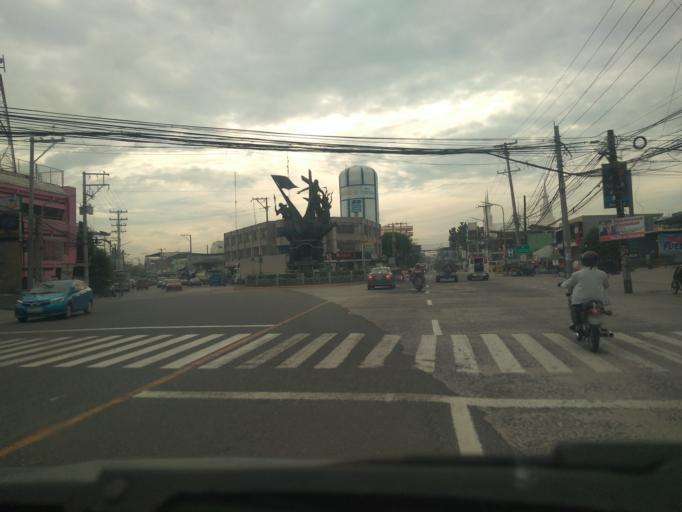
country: PH
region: Central Luzon
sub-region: Province of Pampanga
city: San Fernando
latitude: 15.0337
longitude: 120.6873
